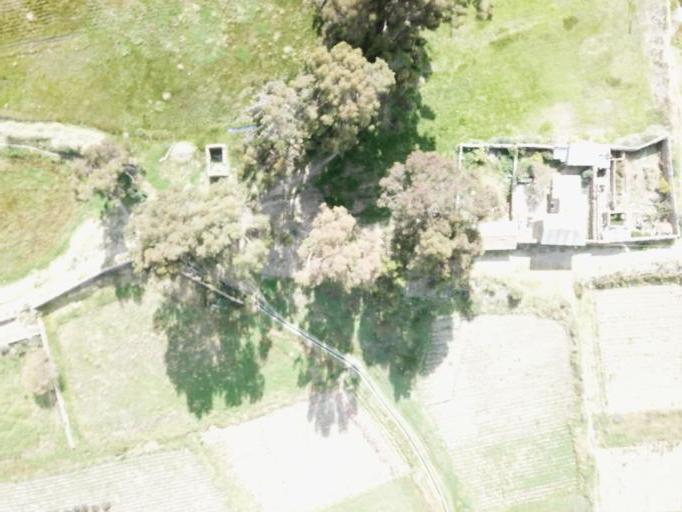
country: BO
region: La Paz
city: Achacachi
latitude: -16.0538
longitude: -68.8161
